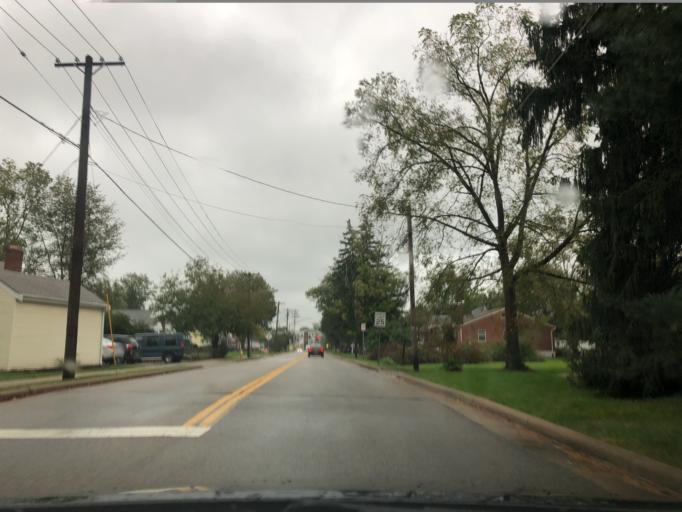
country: US
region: Ohio
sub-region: Hamilton County
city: Blue Ash
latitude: 39.2289
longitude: -84.3801
